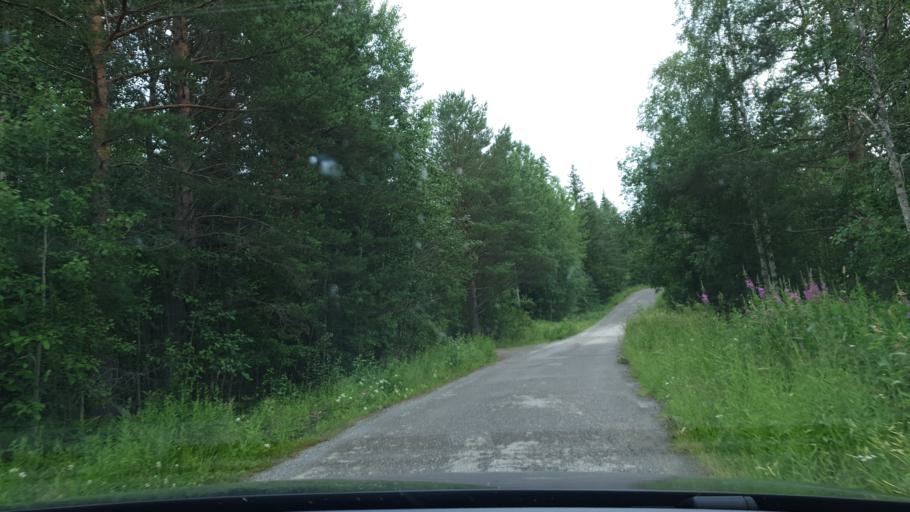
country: SE
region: Gaevleborg
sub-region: Hudiksvalls Kommun
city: Iggesund
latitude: 61.5333
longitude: 17.0124
